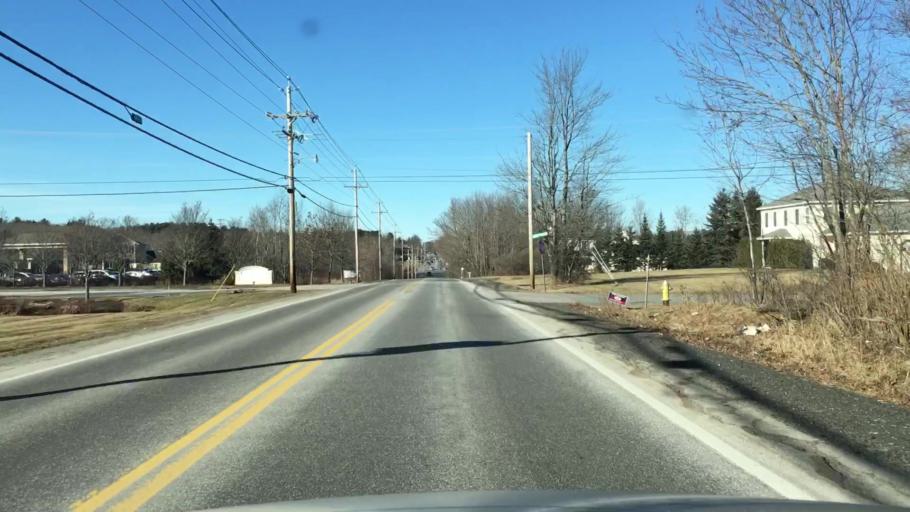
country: US
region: Maine
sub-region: Penobscot County
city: Bangor
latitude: 44.8215
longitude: -68.8052
